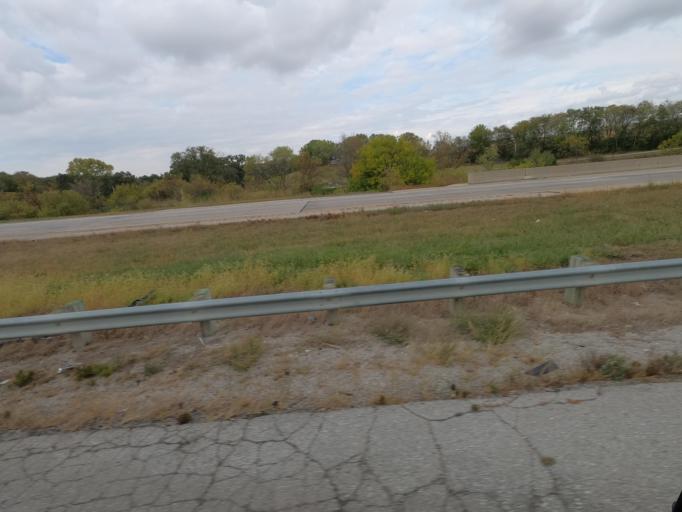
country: US
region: Iowa
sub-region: Polk County
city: Altoona
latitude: 41.5997
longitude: -93.4126
